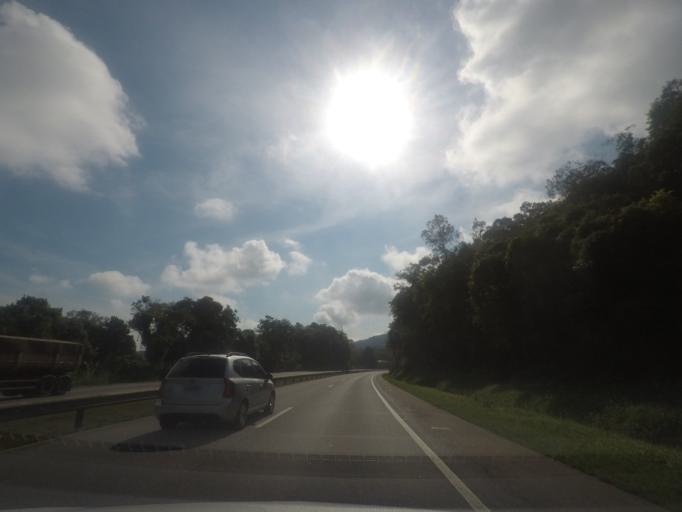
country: BR
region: Parana
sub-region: Antonina
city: Antonina
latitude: -25.5418
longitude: -48.7771
